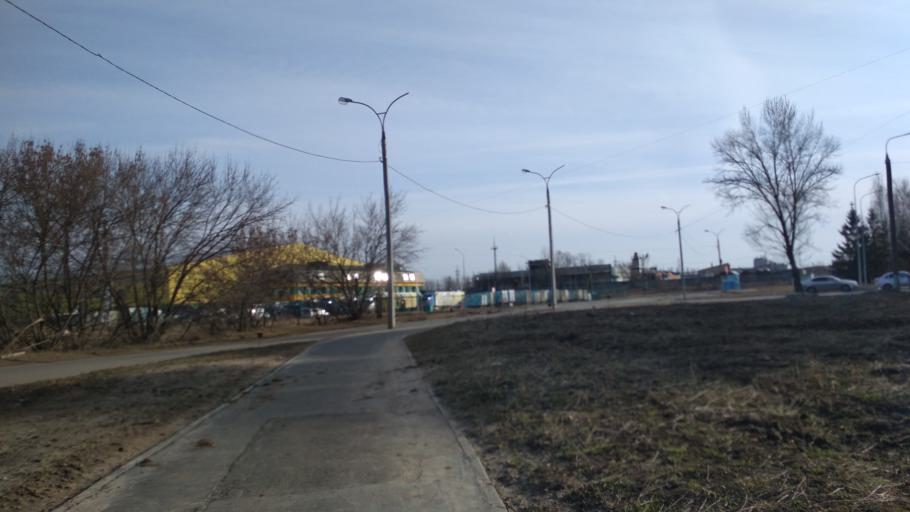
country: RU
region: Chuvashia
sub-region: Cheboksarskiy Rayon
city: Cheboksary
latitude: 56.1349
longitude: 47.3162
